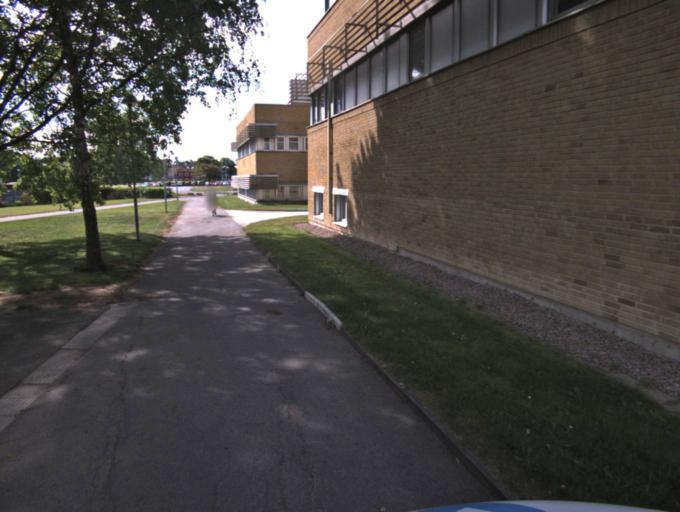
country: SE
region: Skane
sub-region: Kristianstads Kommun
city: Kristianstad
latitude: 56.0314
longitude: 14.1763
